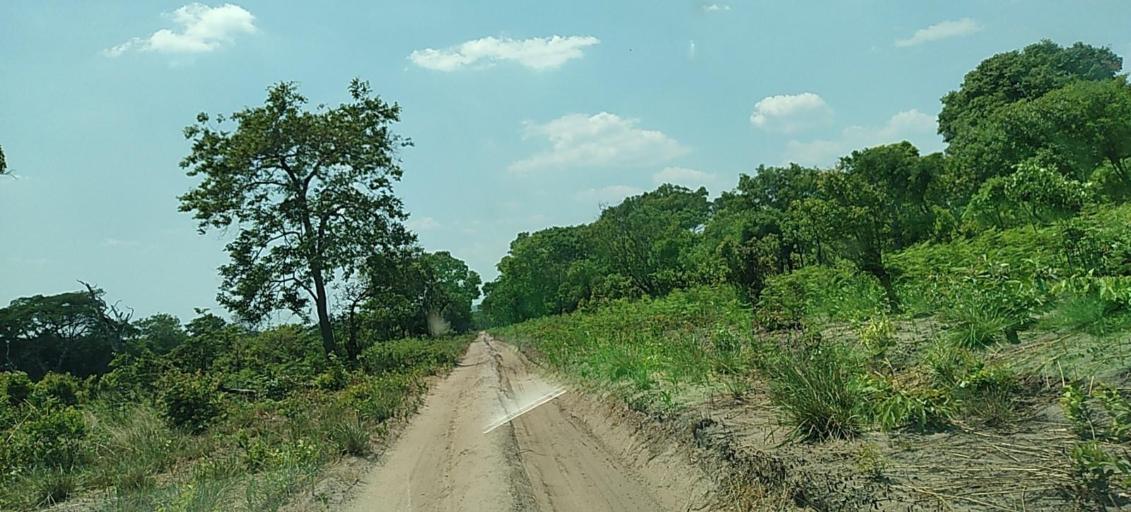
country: CD
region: Katanga
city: Kolwezi
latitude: -11.3095
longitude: 25.2345
